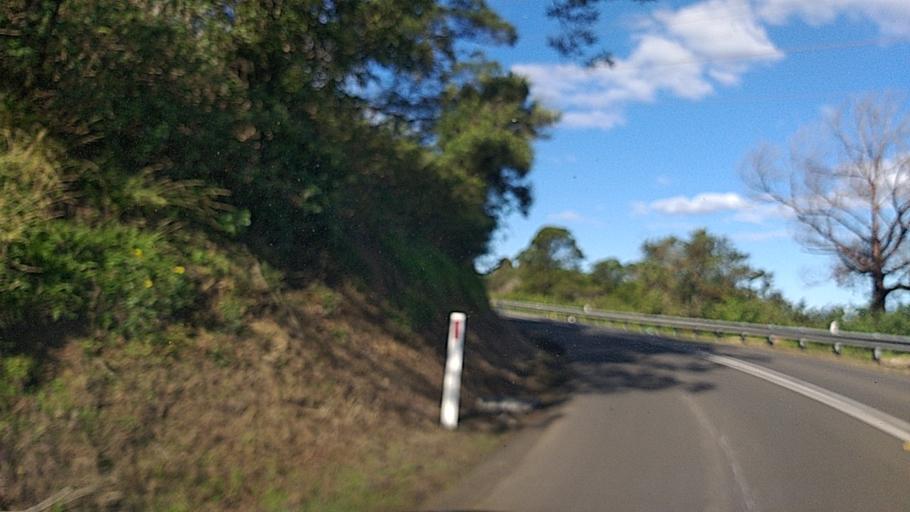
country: AU
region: New South Wales
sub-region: Wollongong
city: Berkeley
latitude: -34.4709
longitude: 150.8467
